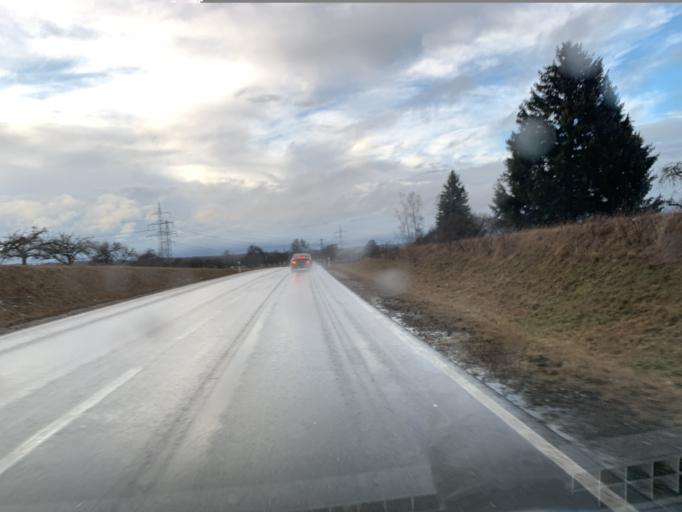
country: DE
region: Baden-Wuerttemberg
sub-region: Regierungsbezirk Stuttgart
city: Magstadt
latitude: 48.7366
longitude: 8.9573
